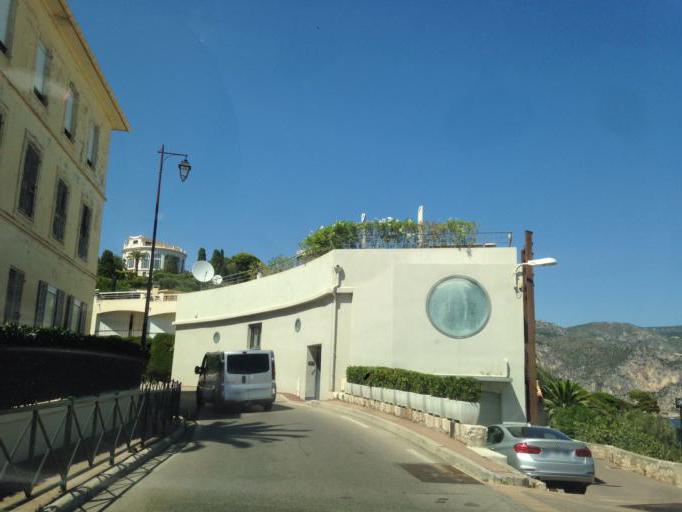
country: FR
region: Provence-Alpes-Cote d'Azur
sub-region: Departement des Alpes-Maritimes
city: Saint-Jean-Cap-Ferrat
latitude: 43.6917
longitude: 7.3328
